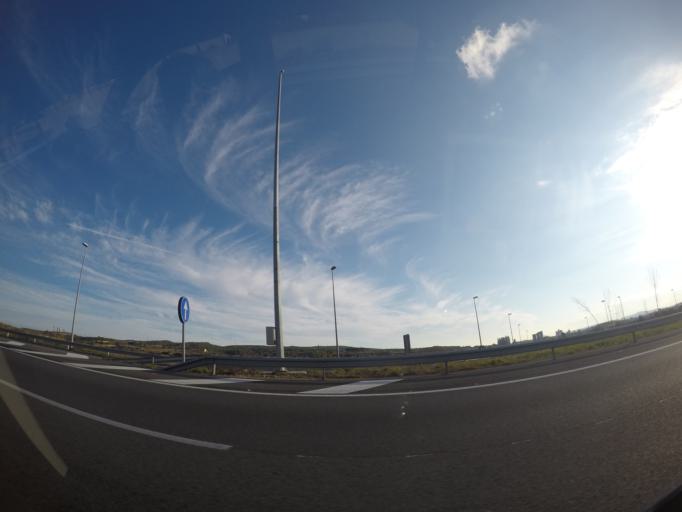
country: ES
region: Catalonia
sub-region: Provincia de Barcelona
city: Vilafranca del Penedes
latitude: 41.3285
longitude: 1.6765
